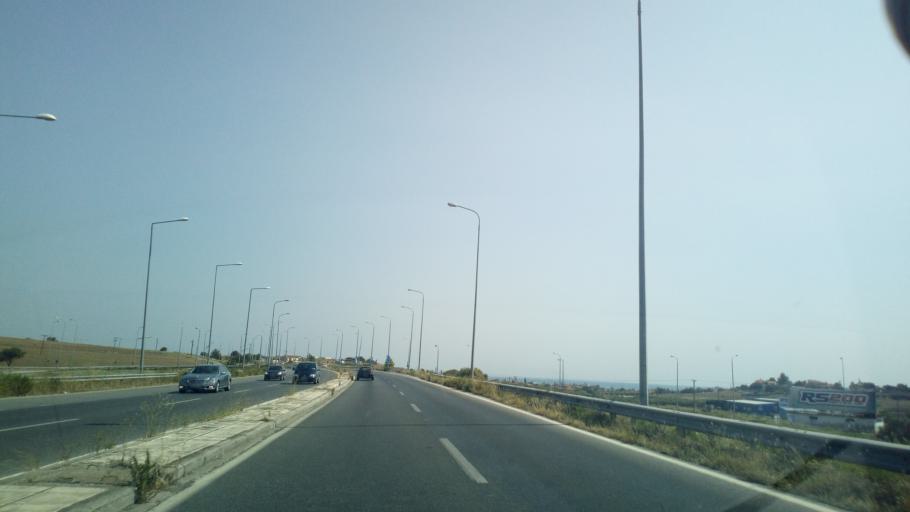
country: GR
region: Central Macedonia
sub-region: Nomos Chalkidikis
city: Nea Plagia
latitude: 40.2882
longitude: 23.1471
